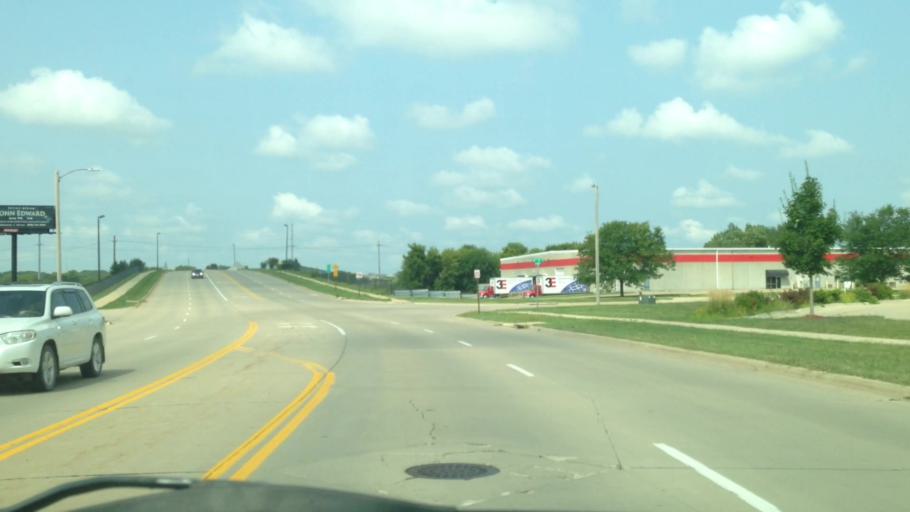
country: US
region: Iowa
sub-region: Linn County
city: Cedar Rapids
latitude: 41.9433
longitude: -91.6837
